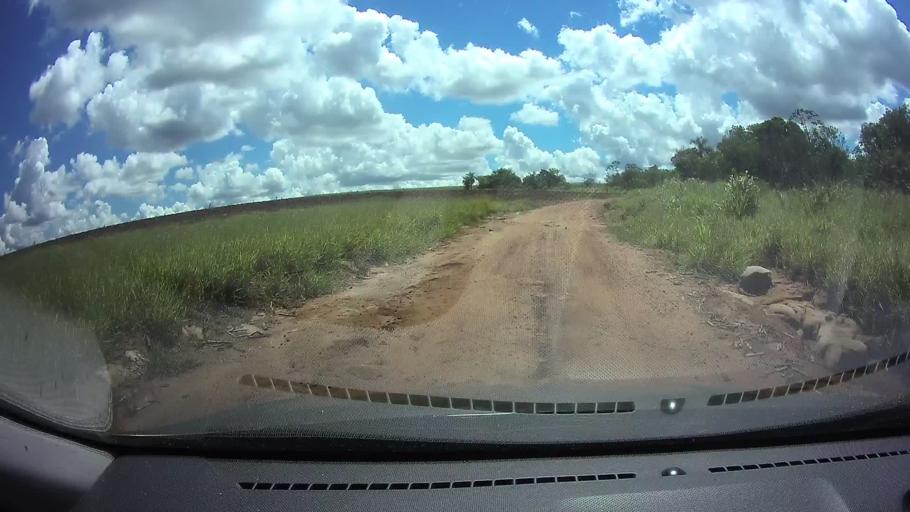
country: PY
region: Paraguari
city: La Colmena
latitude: -25.9665
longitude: -56.7515
